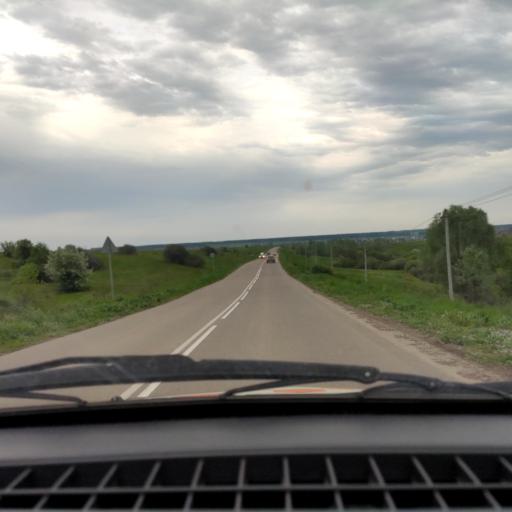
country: RU
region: Bashkortostan
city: Avdon
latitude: 54.5681
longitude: 55.7580
